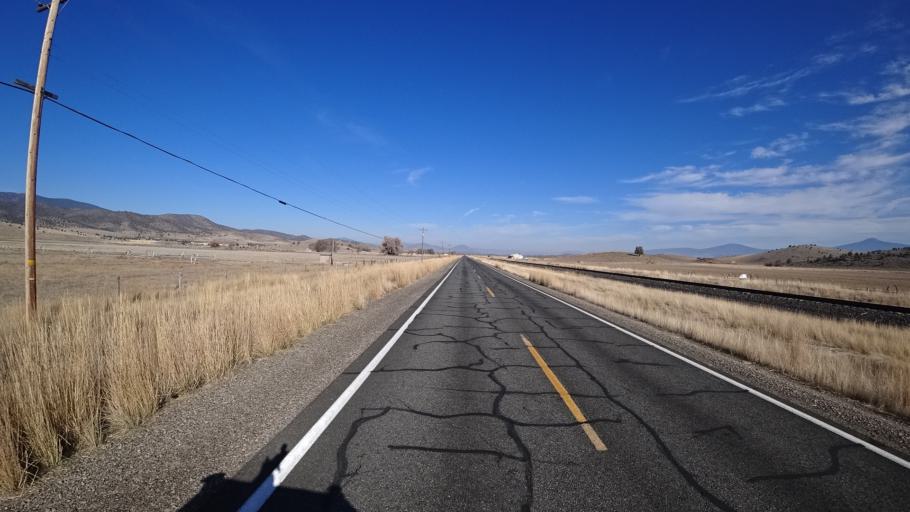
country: US
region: California
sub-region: Siskiyou County
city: Montague
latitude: 41.5788
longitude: -122.5248
